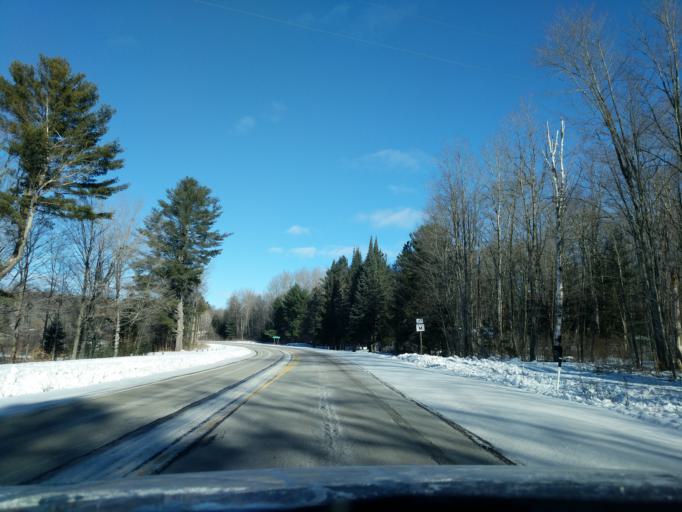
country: US
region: Wisconsin
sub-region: Menominee County
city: Keshena
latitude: 45.1236
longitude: -88.6629
